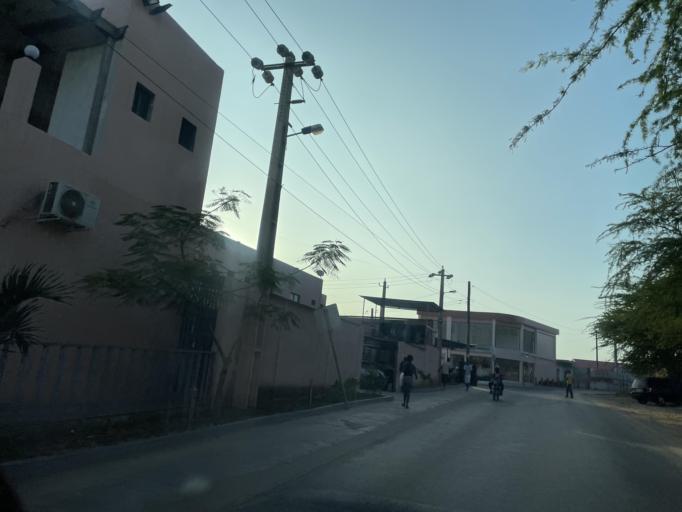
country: AO
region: Luanda
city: Luanda
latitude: -8.9128
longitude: 13.2243
